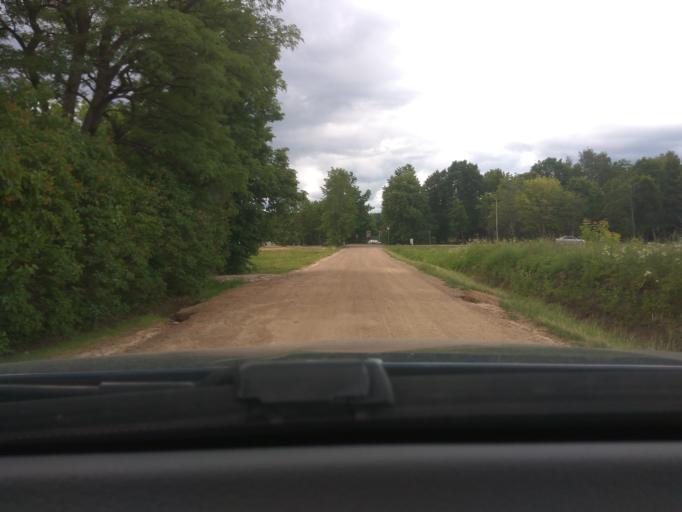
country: LV
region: Kuldigas Rajons
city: Kuldiga
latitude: 56.9718
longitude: 21.9809
